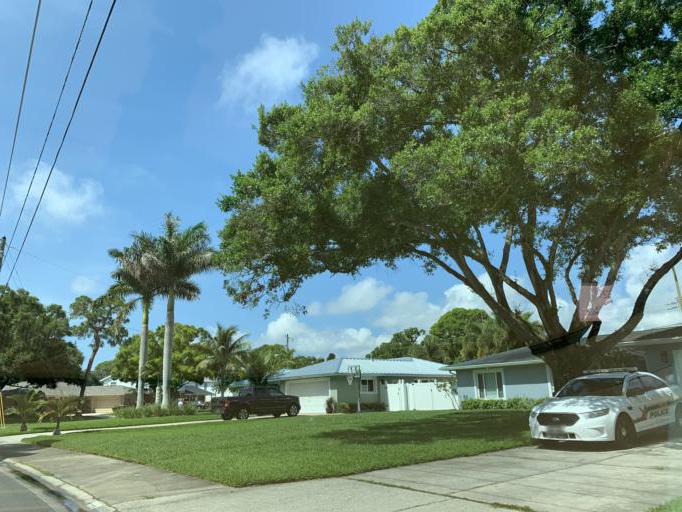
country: US
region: Florida
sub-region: Pinellas County
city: Gandy
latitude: 27.8193
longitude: -82.6092
